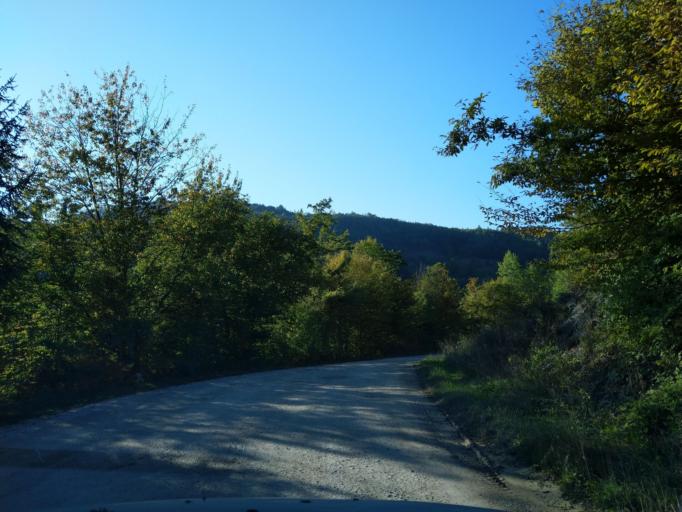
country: RS
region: Central Serbia
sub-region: Moravicki Okrug
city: Ivanjica
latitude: 43.4741
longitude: 20.2392
